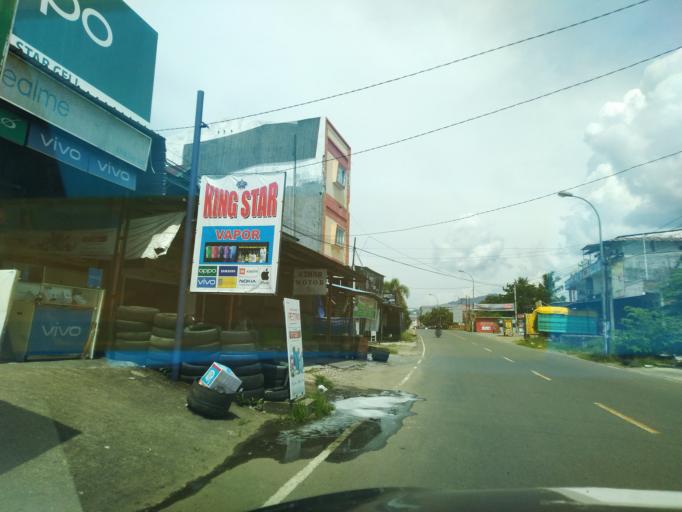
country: ID
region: Sulawesi Barat
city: Mamuju
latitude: -2.6793
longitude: 118.8790
